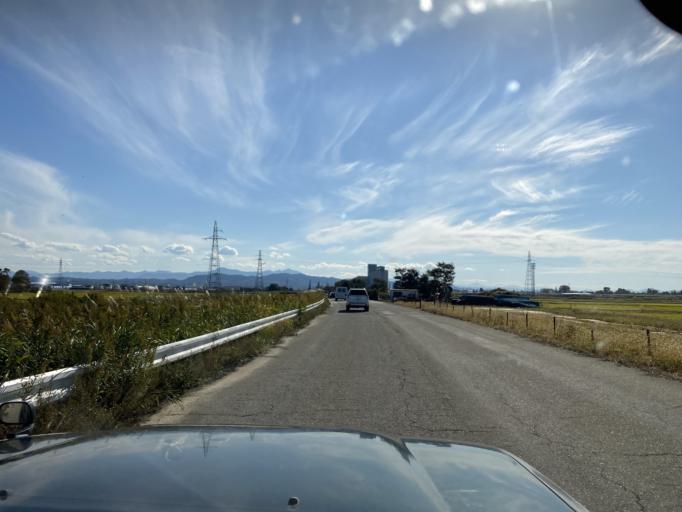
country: JP
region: Niigata
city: Niitsu-honcho
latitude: 37.7992
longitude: 139.0769
